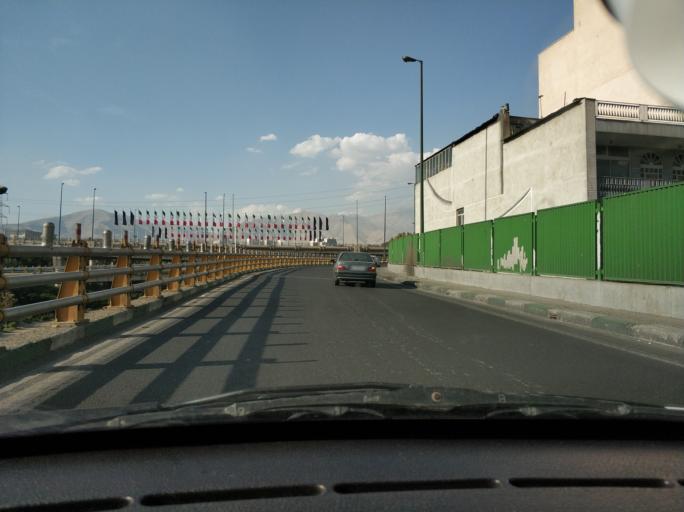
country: IR
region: Tehran
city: Tehran
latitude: 35.7387
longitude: 51.3705
